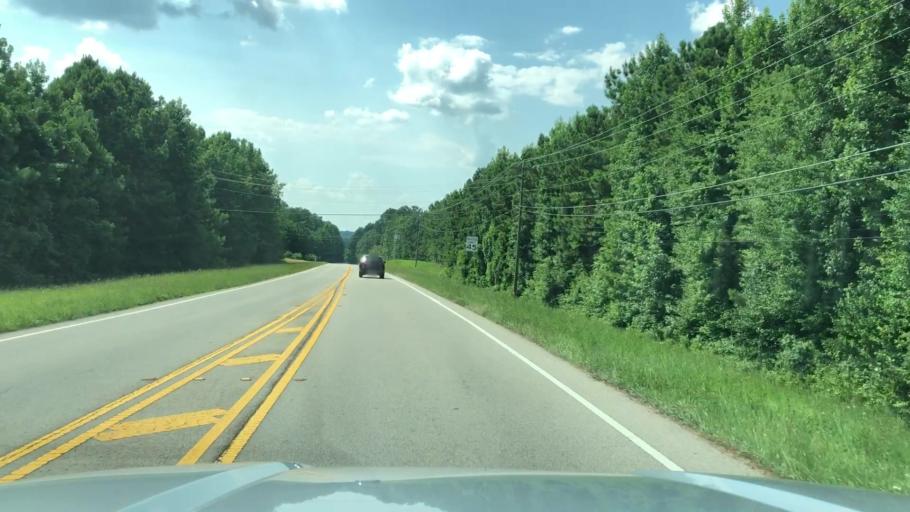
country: US
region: Georgia
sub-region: Paulding County
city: Hiram
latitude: 33.9448
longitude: -84.7670
